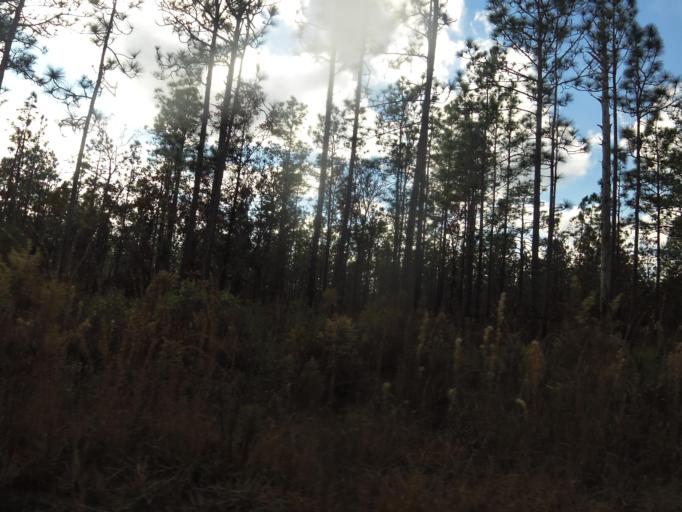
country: US
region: Florida
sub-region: Clay County
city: Middleburg
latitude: 30.1153
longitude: -81.9230
